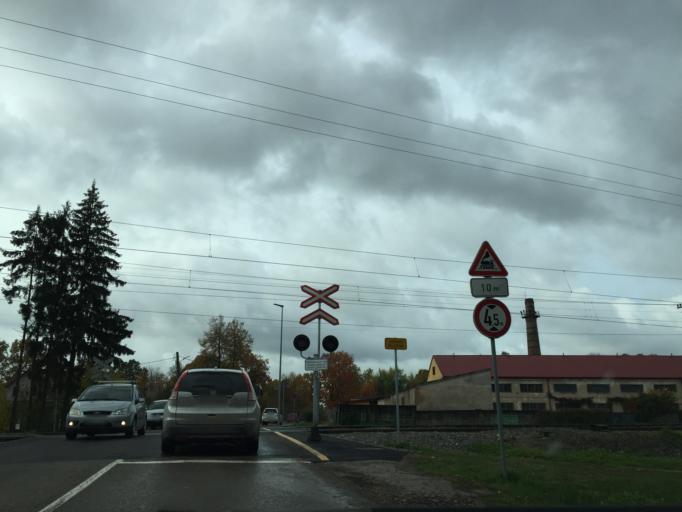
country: LV
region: Ogre
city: Ogre
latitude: 56.8116
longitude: 24.6114
